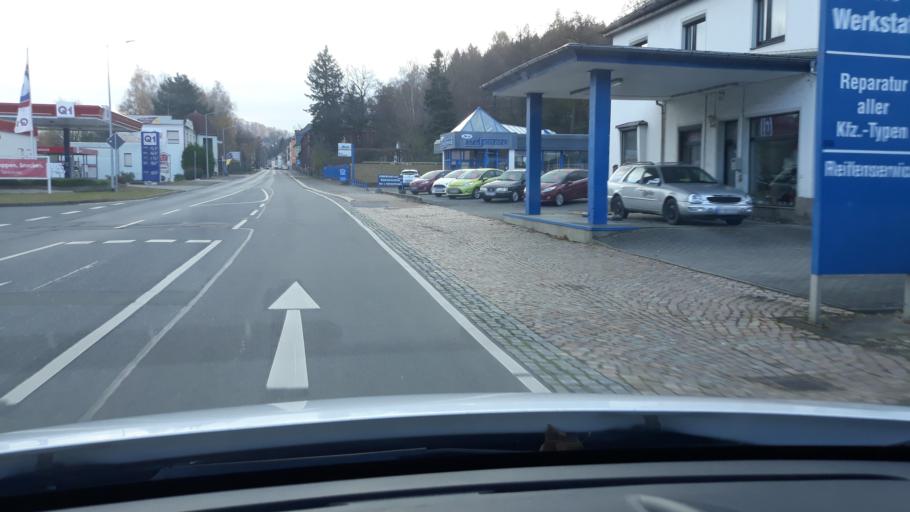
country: DE
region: Saxony
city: Kirchberg
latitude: 50.6303
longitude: 12.5193
